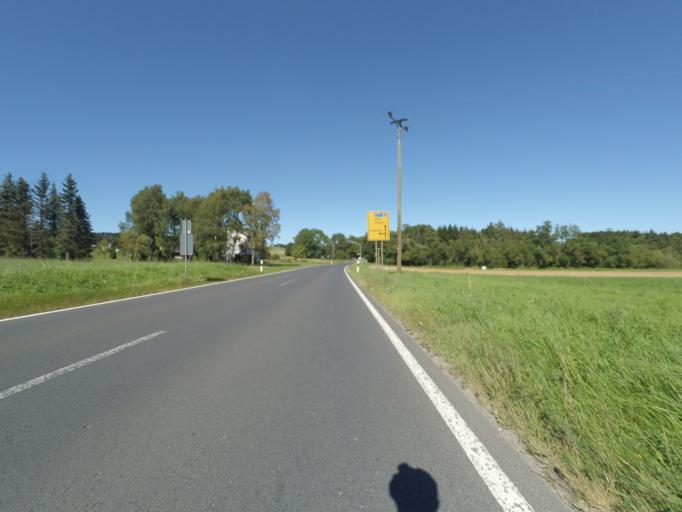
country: DE
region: Rheinland-Pfalz
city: Uxheim
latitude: 50.3236
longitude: 6.7341
